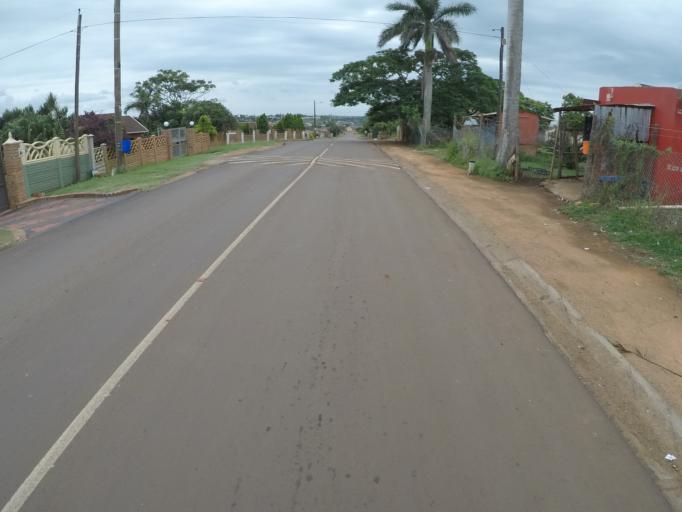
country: ZA
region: KwaZulu-Natal
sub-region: uThungulu District Municipality
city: Empangeni
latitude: -28.7767
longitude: 31.8500
